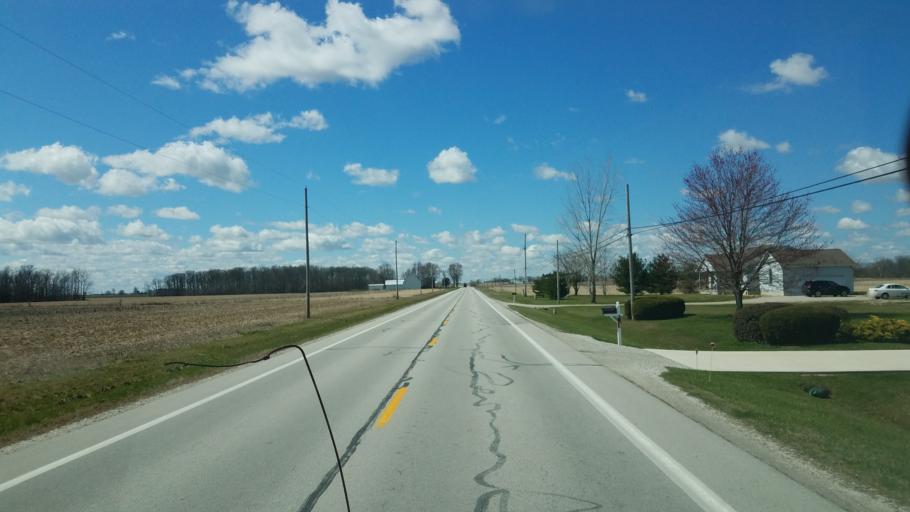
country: US
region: Ohio
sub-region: Seneca County
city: Fostoria
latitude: 41.2039
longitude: -83.3314
